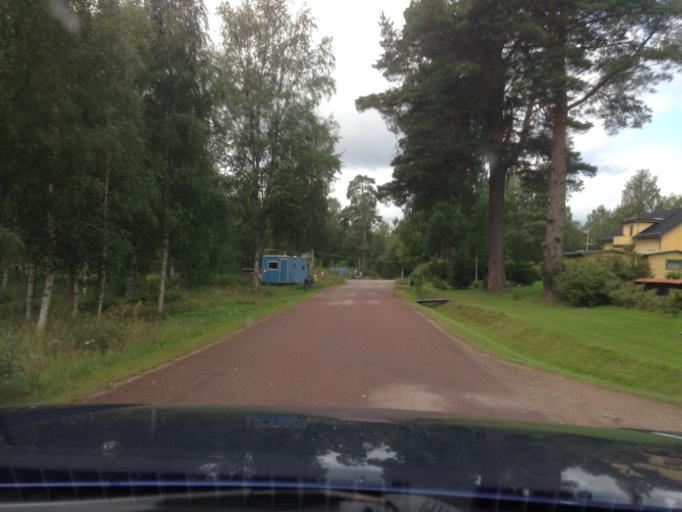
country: SE
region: Dalarna
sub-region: Vansbro Kommun
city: Jarna
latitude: 60.3282
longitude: 14.5345
